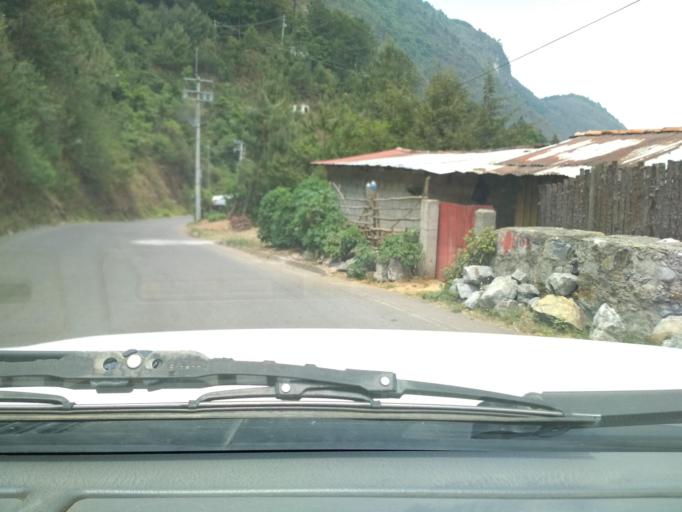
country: MX
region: Veracruz
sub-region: Camerino Z. Mendoza
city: La Cuesta
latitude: 18.7864
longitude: -97.1611
